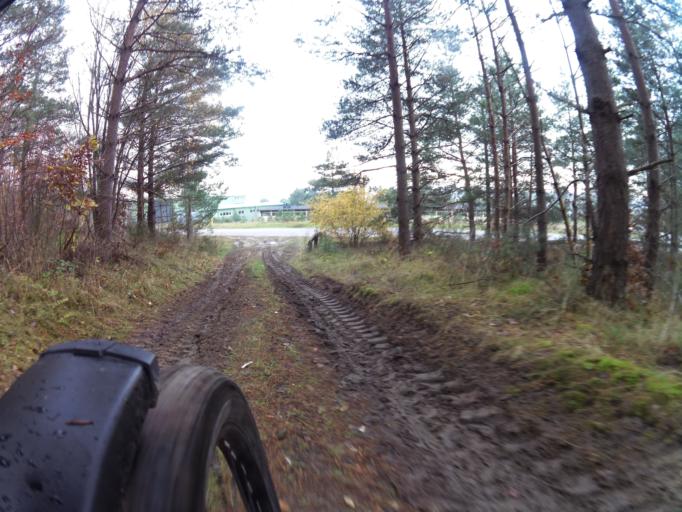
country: PL
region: Pomeranian Voivodeship
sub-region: Powiat pucki
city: Krokowa
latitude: 54.7406
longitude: 18.0984
